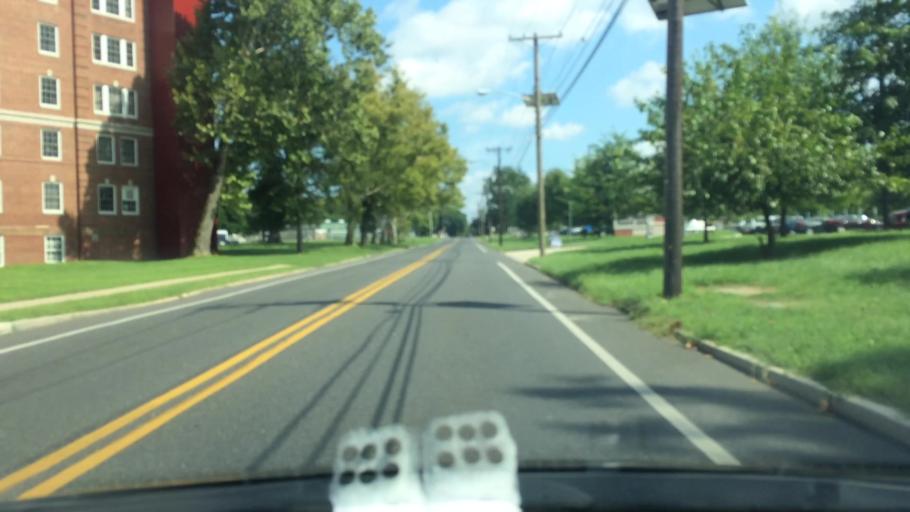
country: US
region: New Jersey
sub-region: Camden County
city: Blackwood
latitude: 39.7853
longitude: -75.0706
